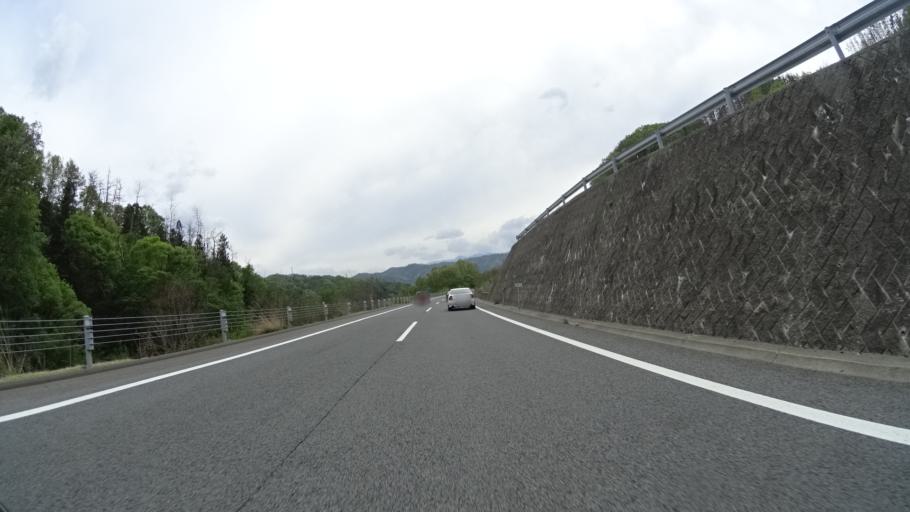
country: JP
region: Nagano
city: Toyoshina
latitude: 36.3578
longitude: 137.9854
